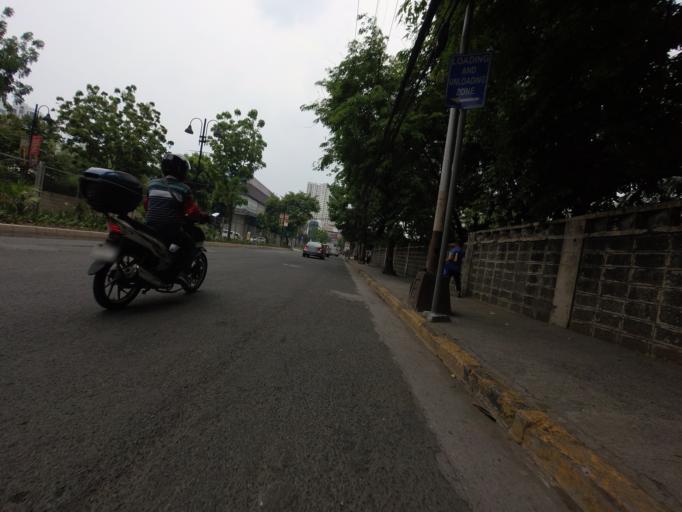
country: PH
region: Metro Manila
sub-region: Pasig
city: Pasig City
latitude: 14.5767
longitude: 121.0620
